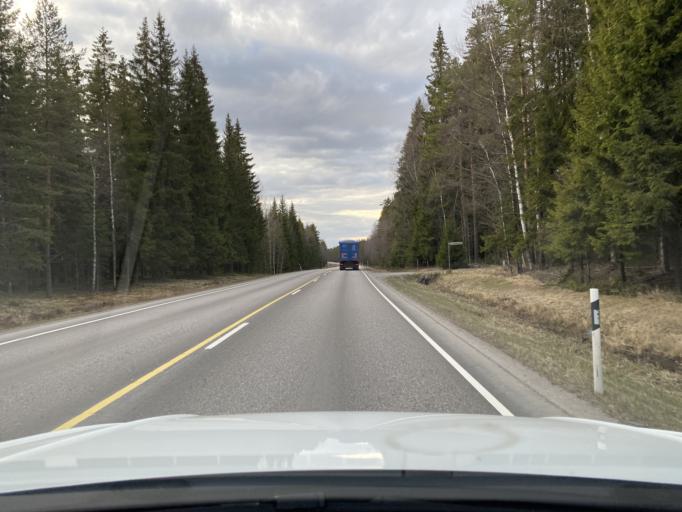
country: FI
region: Uusimaa
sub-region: Helsinki
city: Kaerkoelae
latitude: 60.8063
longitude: 24.0685
